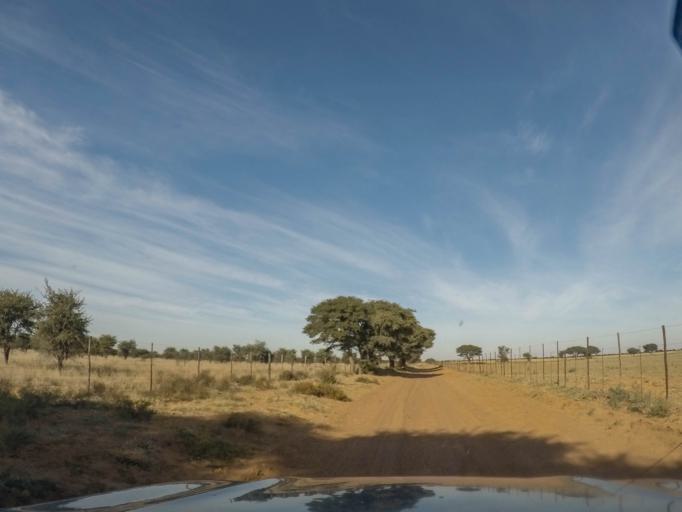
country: BW
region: South East
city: Janeng
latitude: -25.6572
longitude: 25.2509
